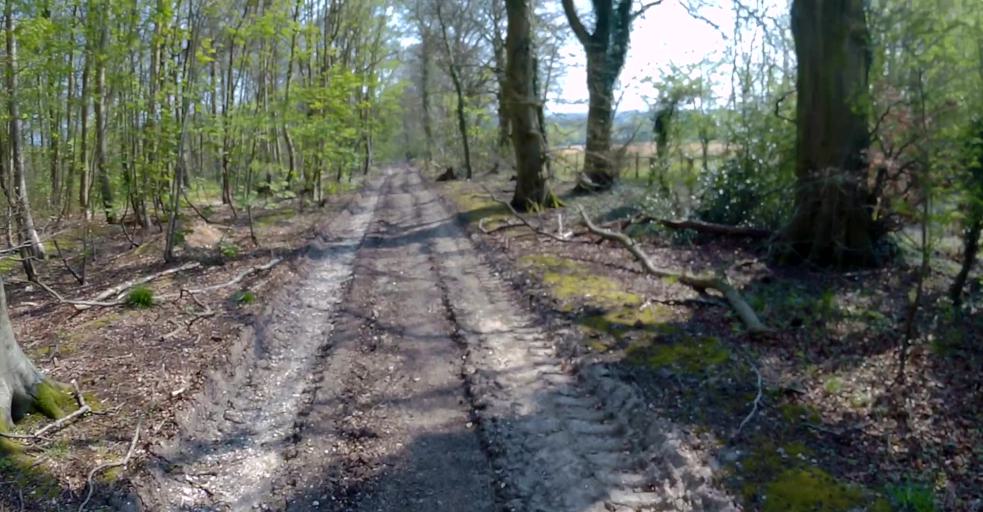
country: GB
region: England
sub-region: Hampshire
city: Overton
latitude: 51.1824
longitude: -1.2422
